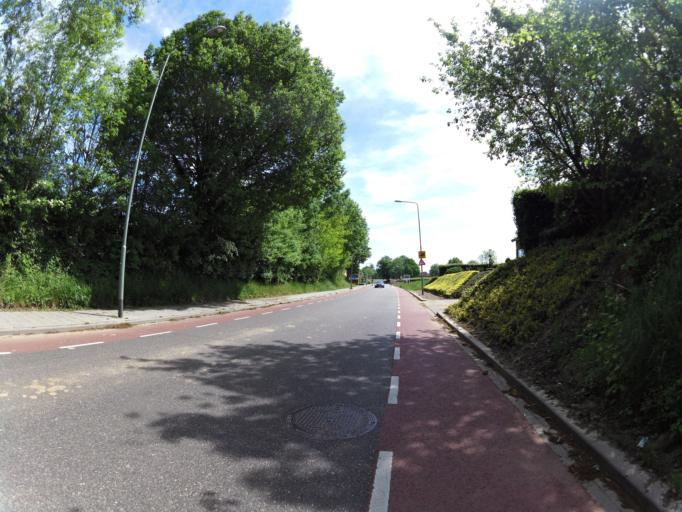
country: NL
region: Limburg
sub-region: Gemeente Simpelveld
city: Simpelveld
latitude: 50.8160
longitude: 5.9970
